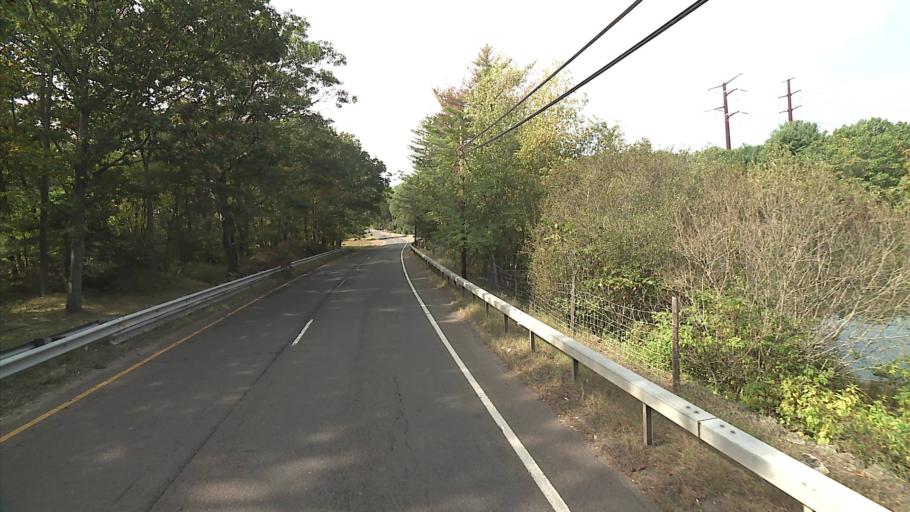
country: US
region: Connecticut
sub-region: New Haven County
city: Orange
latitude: 41.3021
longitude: -72.9847
